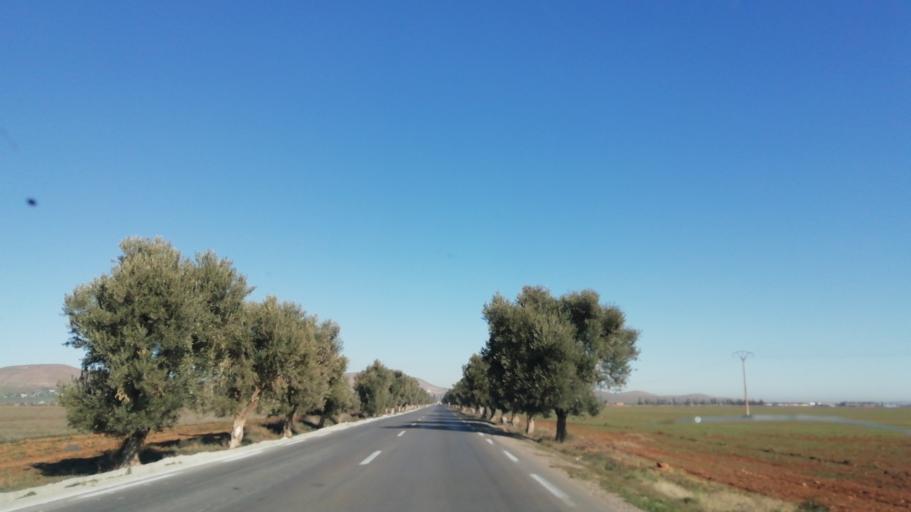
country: DZ
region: Mascara
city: Bou Hanifia el Hamamat
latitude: 35.2017
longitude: 0.1089
